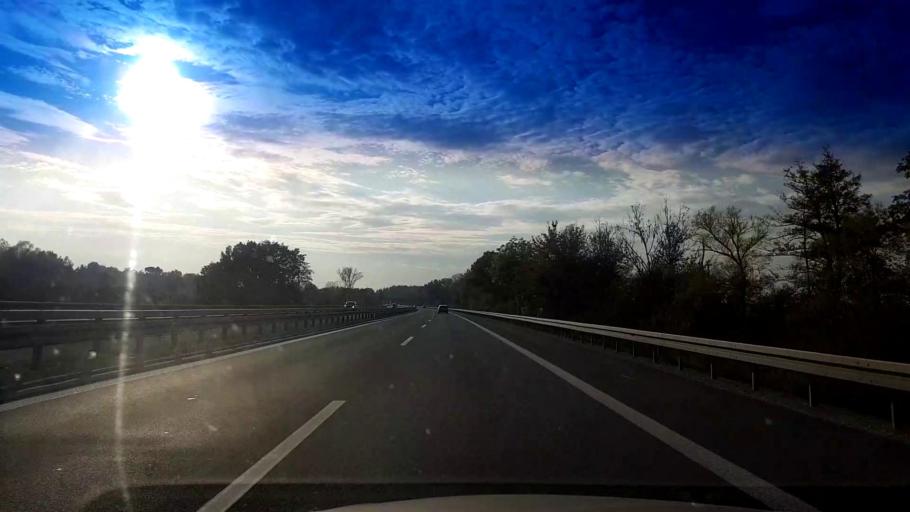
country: DE
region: Bavaria
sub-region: Upper Franconia
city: Gundelsheim
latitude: 49.9311
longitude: 10.9313
